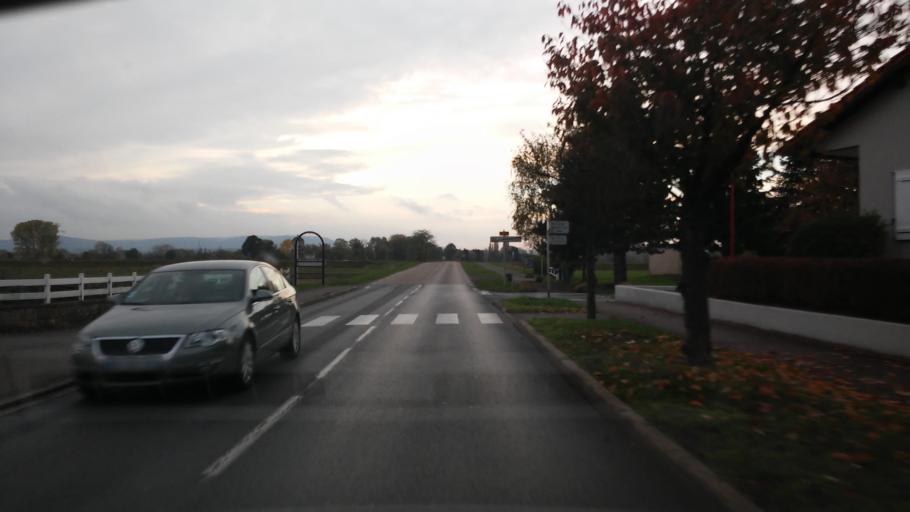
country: FR
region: Lorraine
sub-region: Departement de la Moselle
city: Ay-sur-Moselle
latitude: 49.2447
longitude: 6.2025
